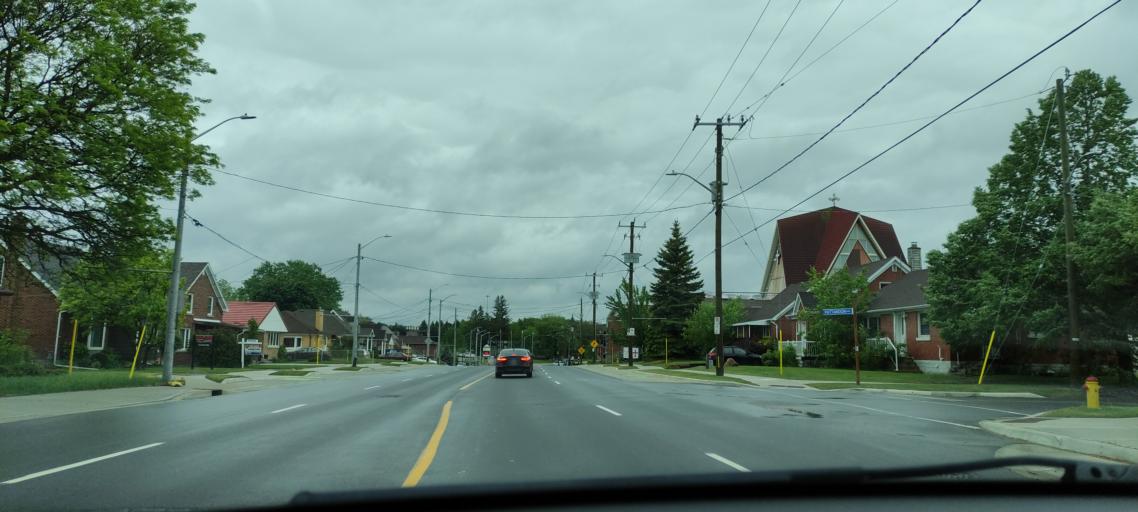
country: CA
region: Ontario
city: Kitchener
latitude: 43.4339
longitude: -80.4788
